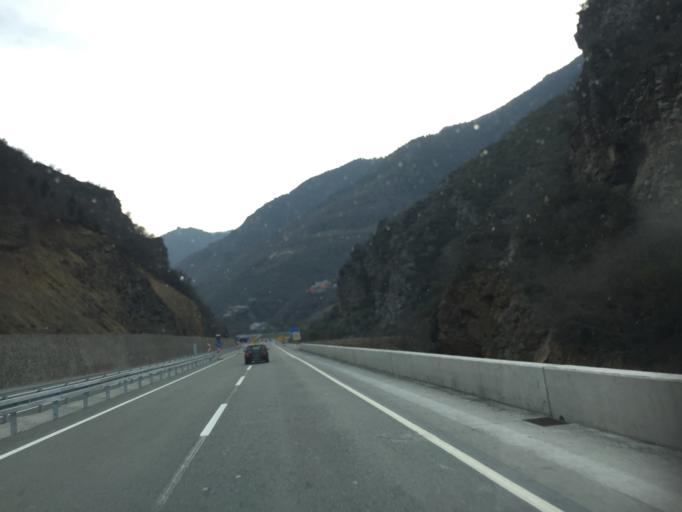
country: TR
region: Trabzon
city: Macka
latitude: 40.7841
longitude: 39.5748
